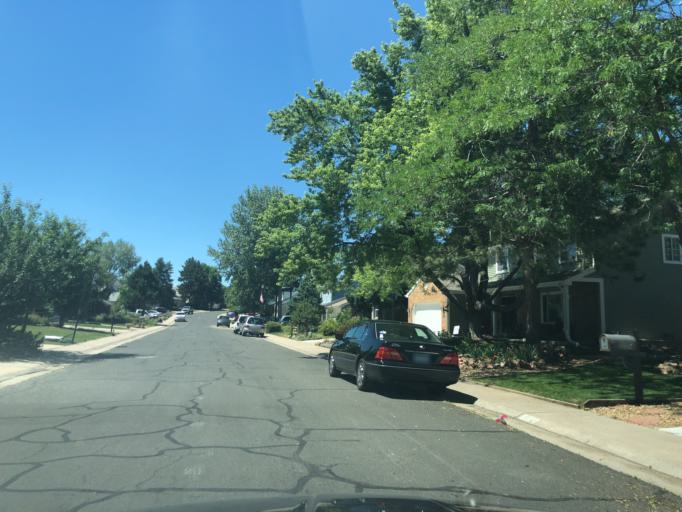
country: US
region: Colorado
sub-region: Arapahoe County
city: Dove Valley
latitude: 39.6158
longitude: -104.7839
